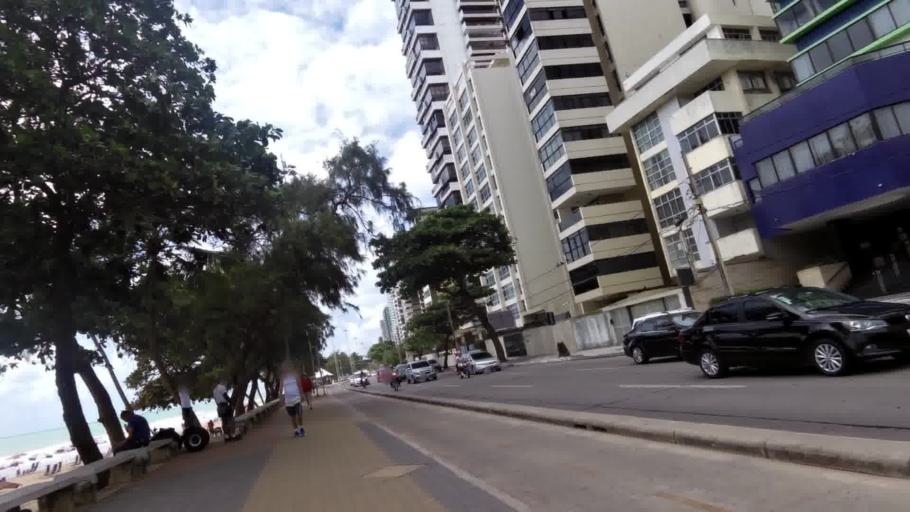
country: BR
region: Pernambuco
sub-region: Recife
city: Recife
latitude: -8.1270
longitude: -34.8978
